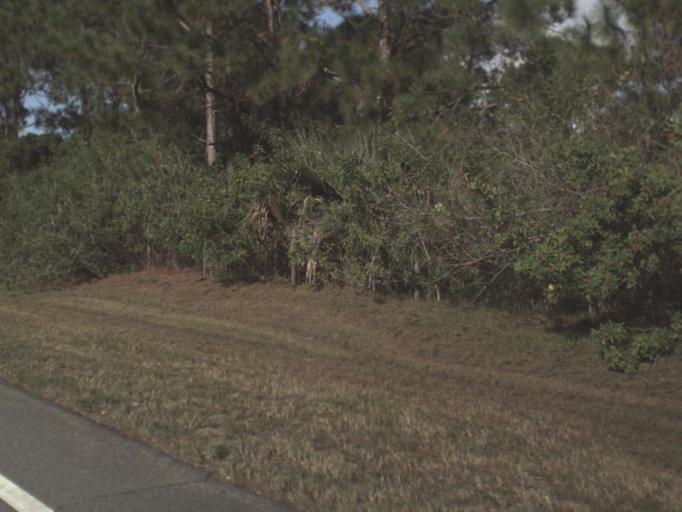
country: US
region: Florida
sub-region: Volusia County
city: South Daytona
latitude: 29.1534
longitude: -81.0641
